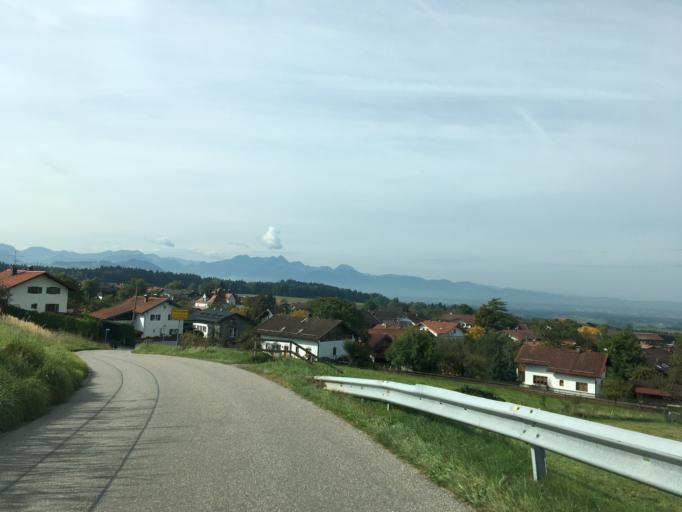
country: DE
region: Bavaria
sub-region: Upper Bavaria
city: Frasdorf
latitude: 47.8355
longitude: 12.2569
